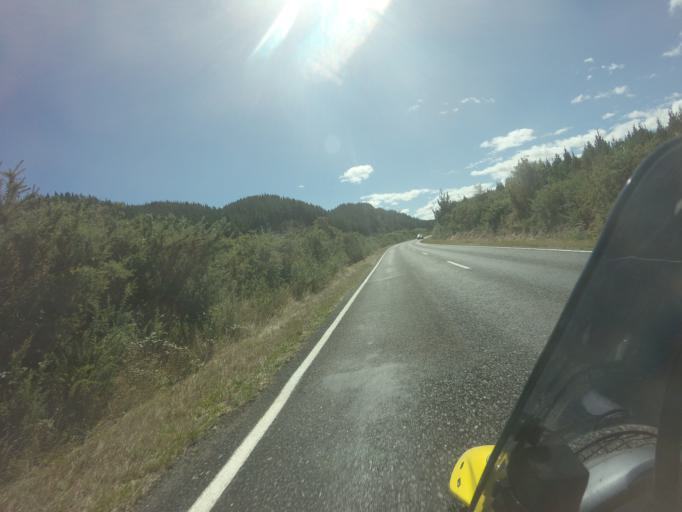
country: NZ
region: Bay of Plenty
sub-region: Kawerau District
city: Kawerau
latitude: -38.2591
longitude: 176.8195
